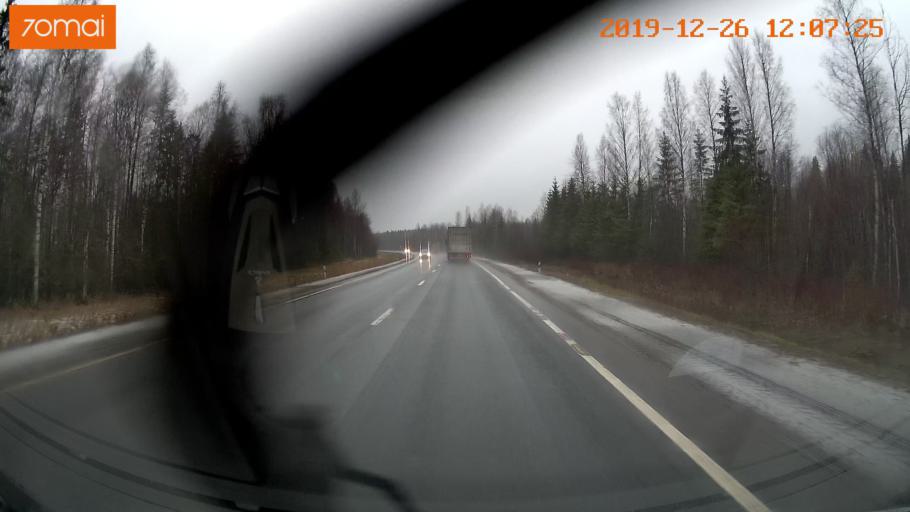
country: RU
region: Vologda
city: Tonshalovo
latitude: 59.2902
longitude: 38.0326
